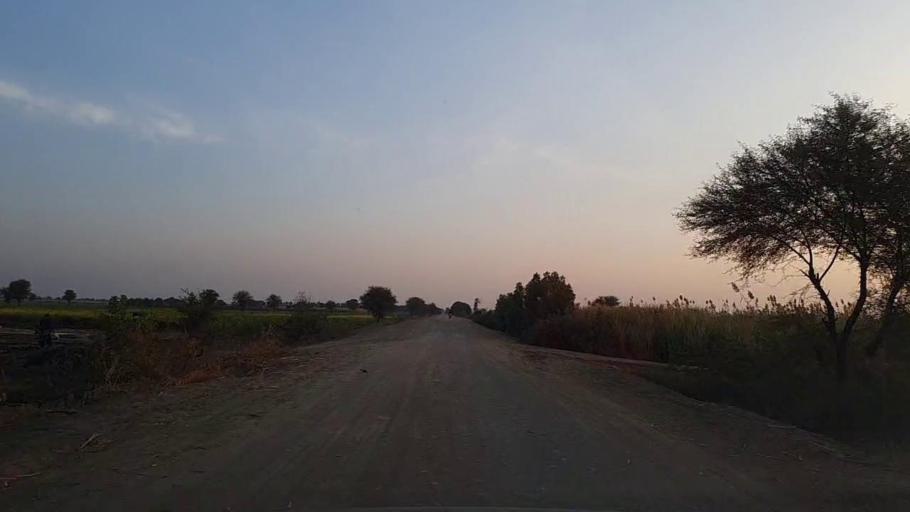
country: PK
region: Sindh
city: Tando Mittha Khan
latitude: 25.9705
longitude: 69.1105
